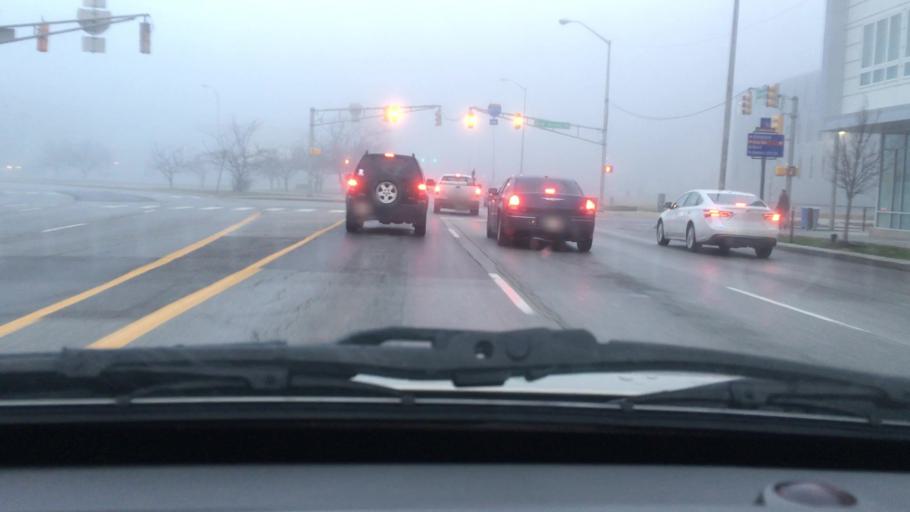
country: US
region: Indiana
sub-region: Marion County
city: Indianapolis
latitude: 39.7670
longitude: -86.1504
